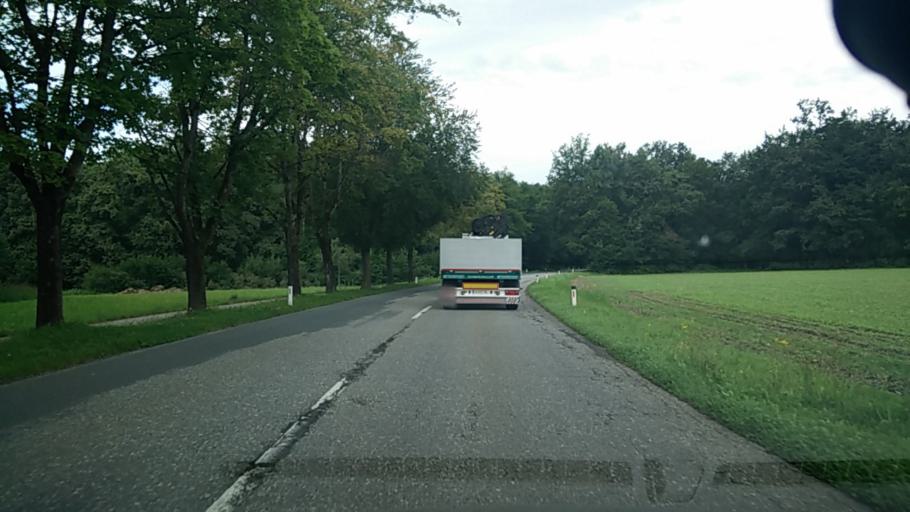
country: AT
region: Carinthia
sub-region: Klagenfurt am Woerthersee
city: Klagenfurt am Woerthersee
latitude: 46.6083
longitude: 14.2644
